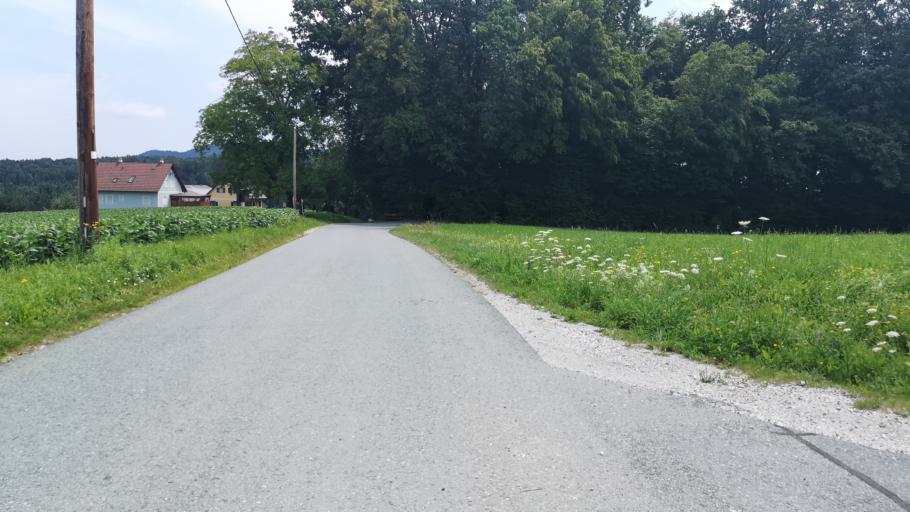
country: AT
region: Styria
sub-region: Politischer Bezirk Leibnitz
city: Weitendorf
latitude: 46.8724
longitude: 15.4606
